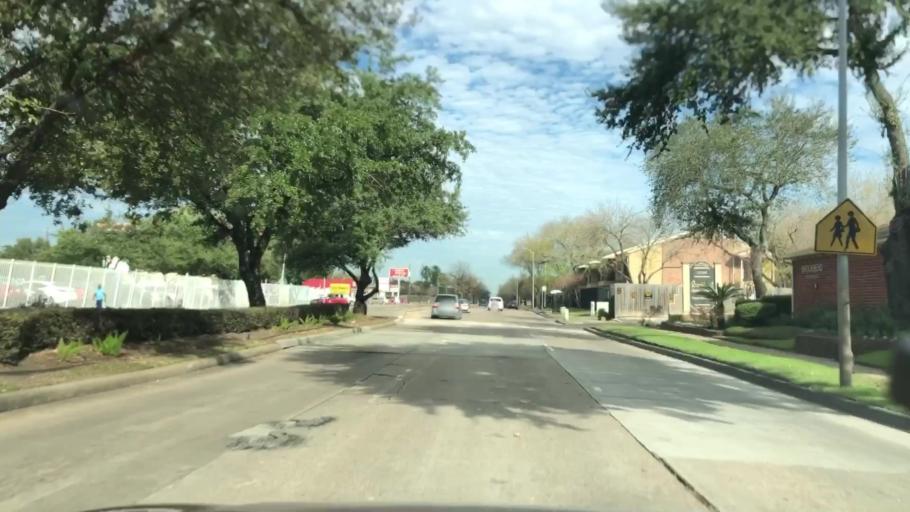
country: US
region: Texas
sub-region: Fort Bend County
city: Missouri City
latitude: 29.6463
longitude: -95.5083
